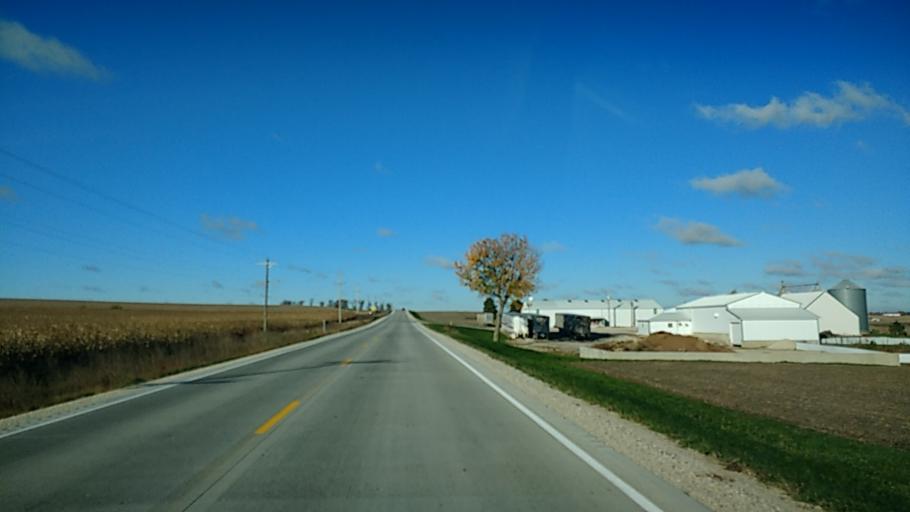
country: US
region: Iowa
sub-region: Ida County
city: Holstein
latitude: 42.5040
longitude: -95.3948
